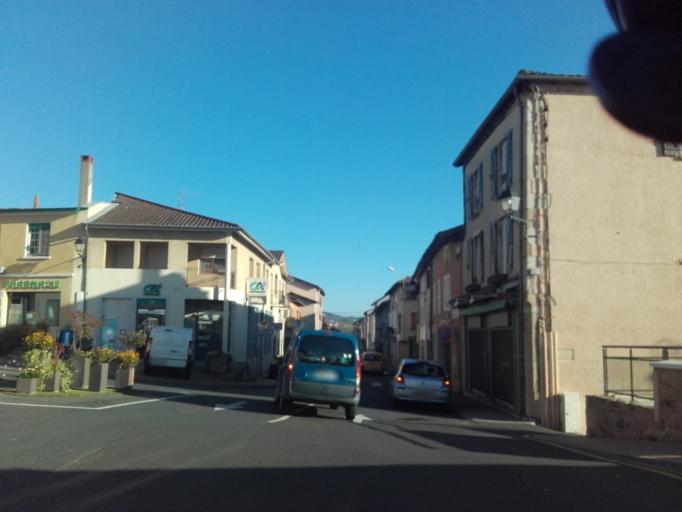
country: FR
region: Rhone-Alpes
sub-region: Departement du Rhone
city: Villie-Morgon
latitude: 46.1616
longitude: 4.6802
